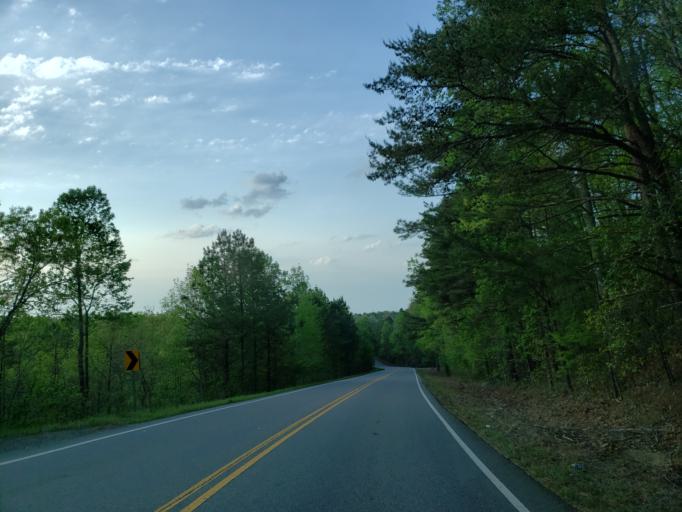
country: US
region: Georgia
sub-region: Cherokee County
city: Ball Ground
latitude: 34.2715
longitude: -84.3712
